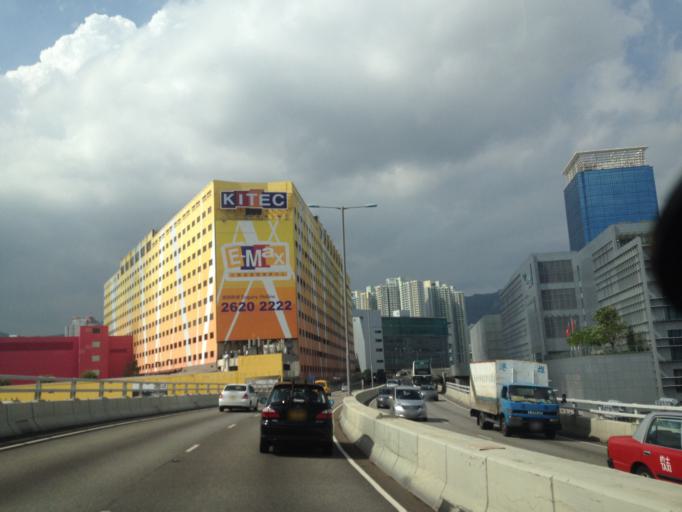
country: HK
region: Kowloon City
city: Kowloon
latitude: 22.3220
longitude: 114.2046
